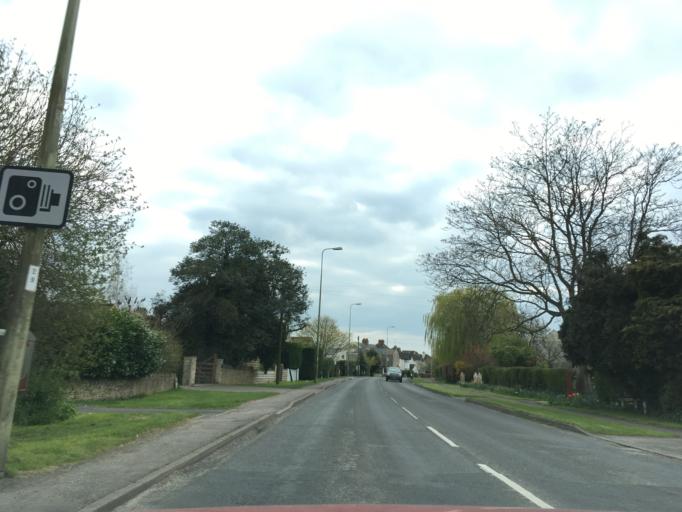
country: GB
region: England
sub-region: Oxfordshire
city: Witney
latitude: 51.7953
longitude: -1.4688
